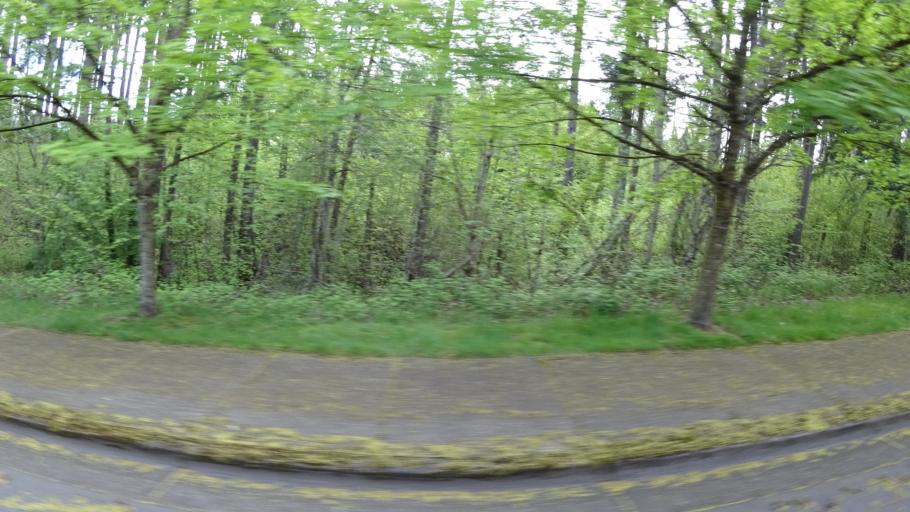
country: US
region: Oregon
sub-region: Washington County
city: Beaverton
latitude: 45.4477
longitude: -122.8380
